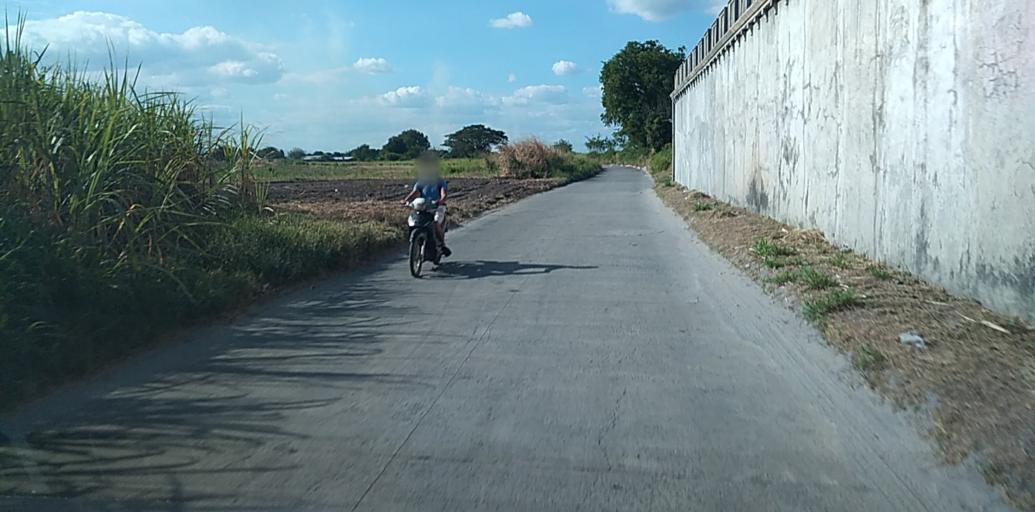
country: PH
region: Central Luzon
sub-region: Province of Pampanga
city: Acli
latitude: 15.1145
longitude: 120.6466
